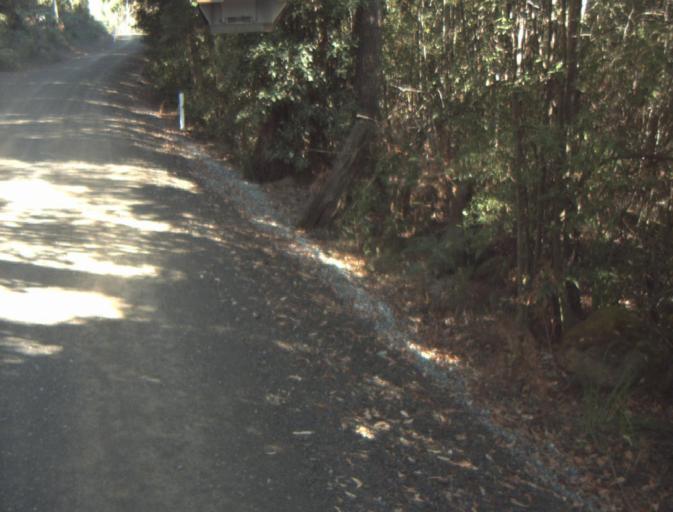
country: AU
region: Tasmania
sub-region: Launceston
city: Mayfield
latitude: -41.3016
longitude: 147.1904
